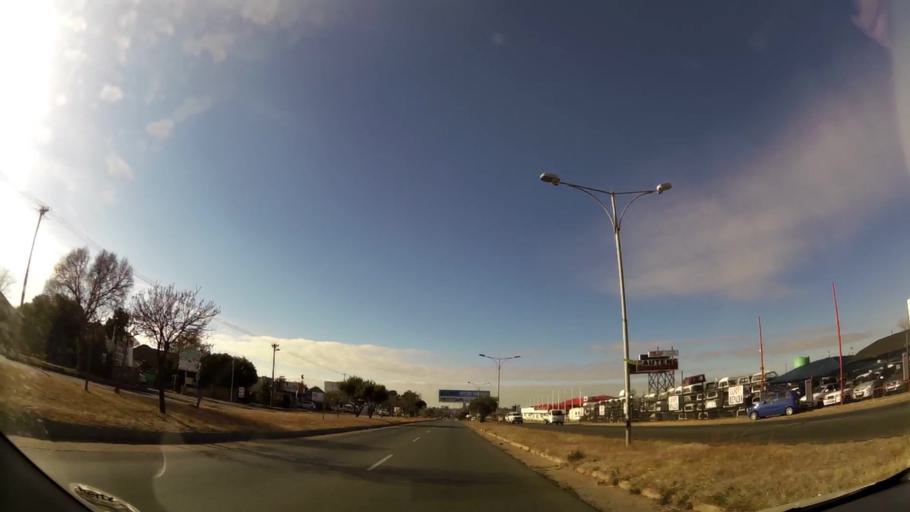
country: ZA
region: Gauteng
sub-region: West Rand District Municipality
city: Krugersdorp
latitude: -26.1219
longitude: 27.8210
